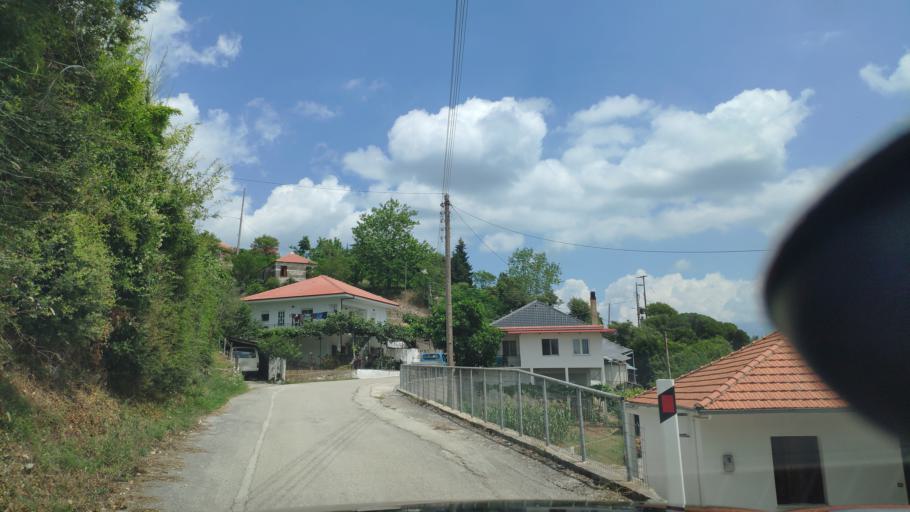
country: GR
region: Epirus
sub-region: Nomos Artas
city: Agios Dimitrios
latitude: 39.3257
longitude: 20.9987
